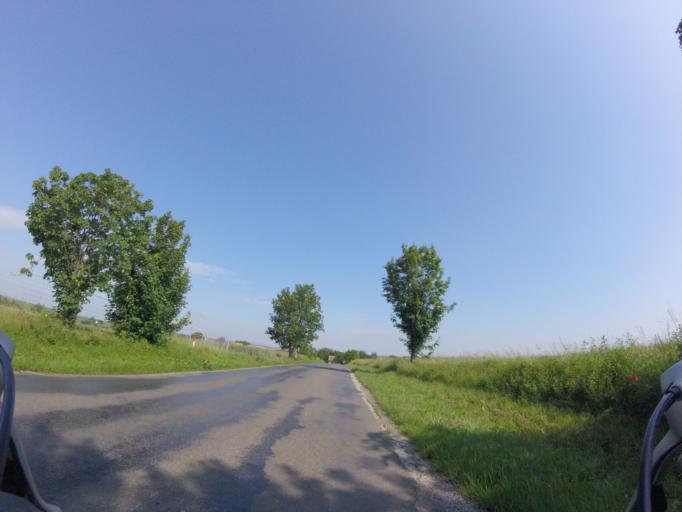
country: HU
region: Baranya
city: Siklos
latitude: 45.9254
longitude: 18.3694
